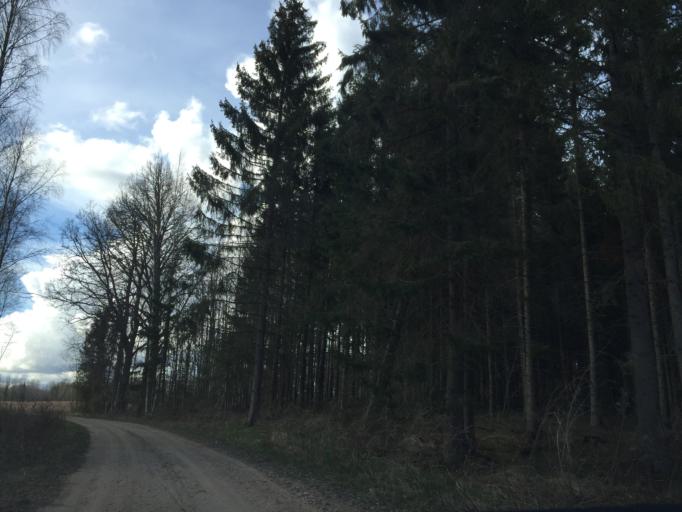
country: LV
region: Burtnieki
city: Matisi
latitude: 57.6157
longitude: 25.0030
